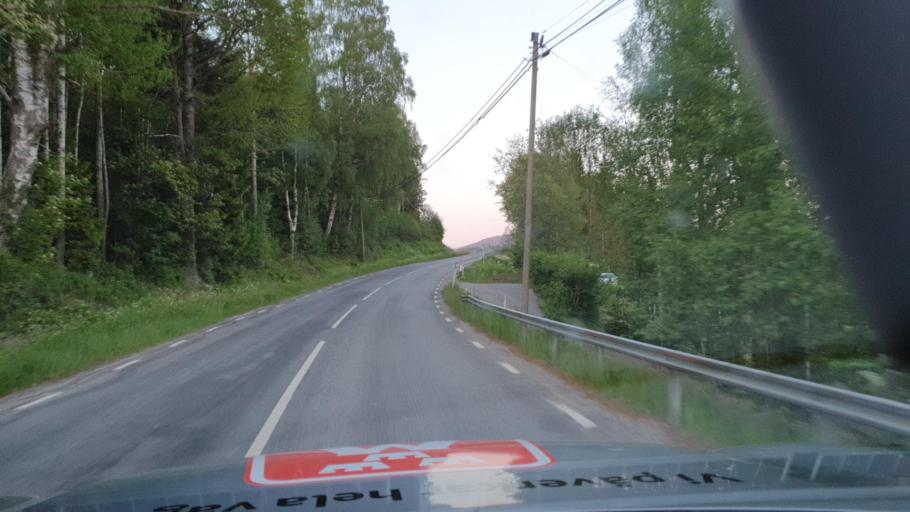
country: SE
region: Vaesternorrland
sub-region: OErnskoeldsviks Kommun
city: Kopmanholmen
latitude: 63.2334
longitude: 18.5928
